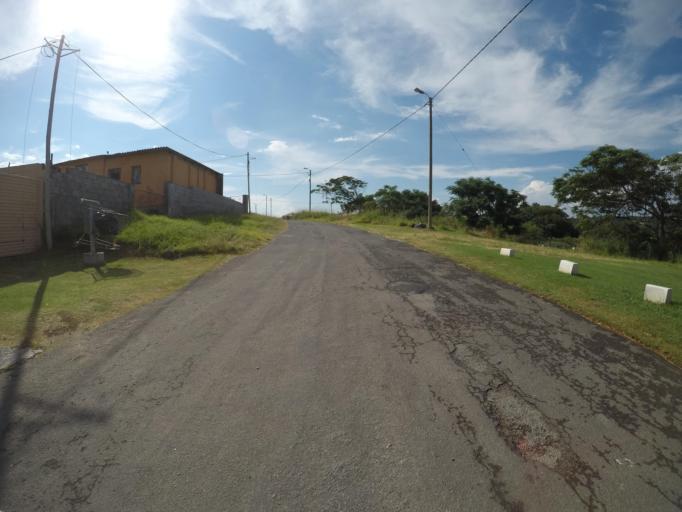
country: ZA
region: Eastern Cape
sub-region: Buffalo City Metropolitan Municipality
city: East London
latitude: -33.0231
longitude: 27.8818
